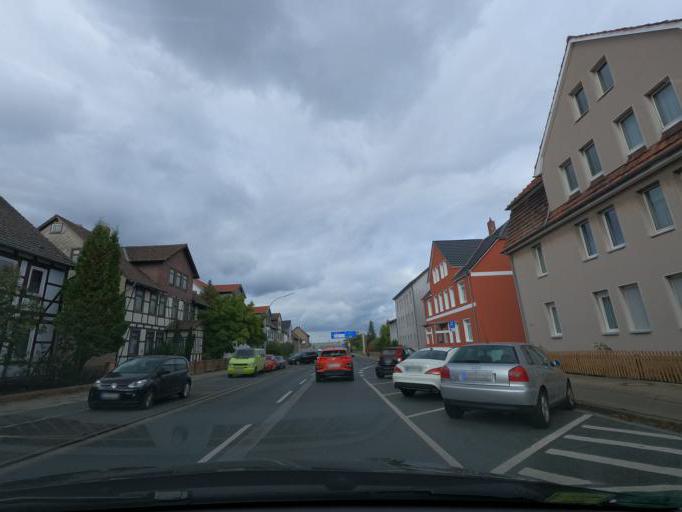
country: DE
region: Lower Saxony
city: Leiferde
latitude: 52.2253
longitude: 10.5040
